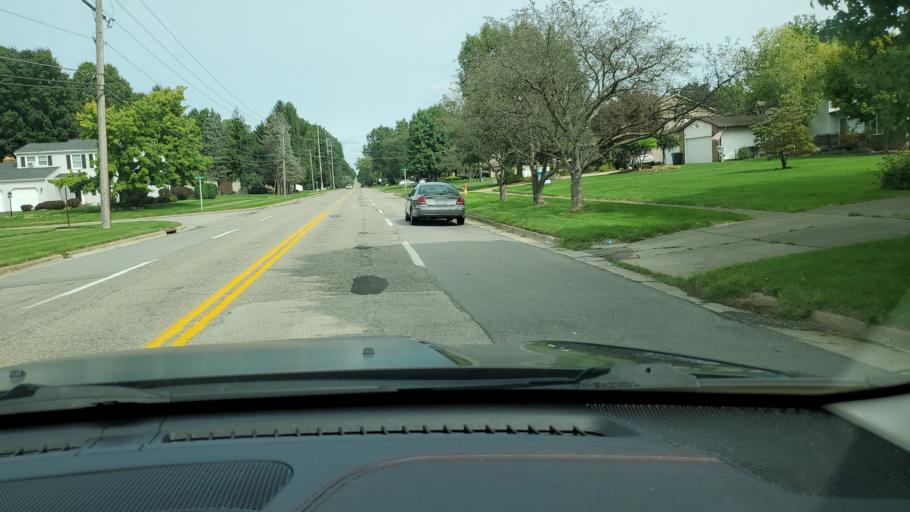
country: US
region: Ohio
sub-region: Mahoning County
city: Boardman
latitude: 40.9975
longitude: -80.6723
